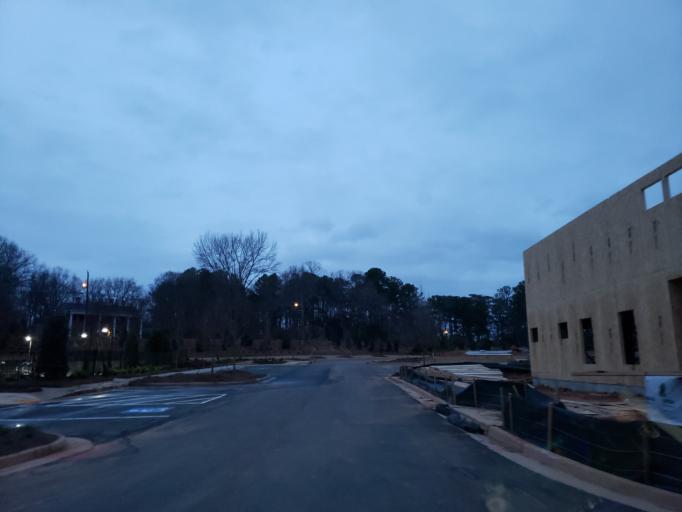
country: US
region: Georgia
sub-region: Cobb County
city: Mableton
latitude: 33.8397
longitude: -84.5808
